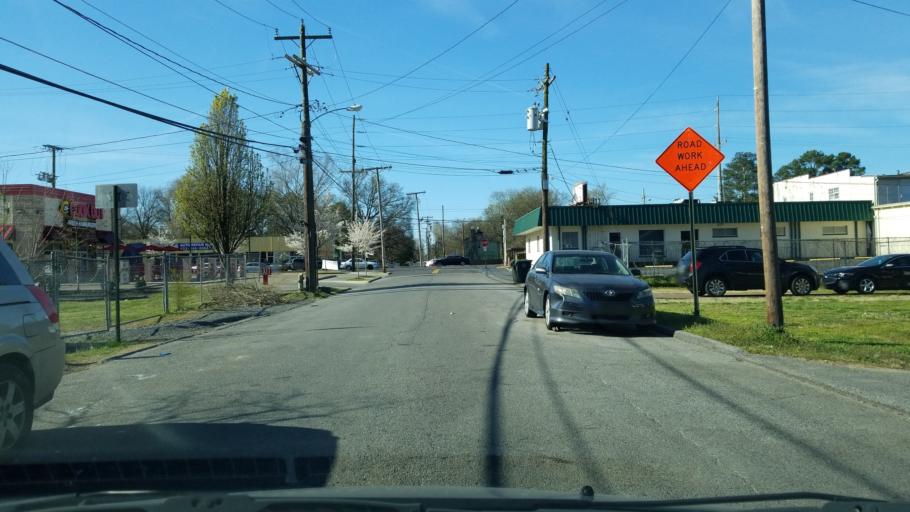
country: US
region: Tennessee
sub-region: Hamilton County
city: East Ridge
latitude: 35.0128
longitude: -85.2257
